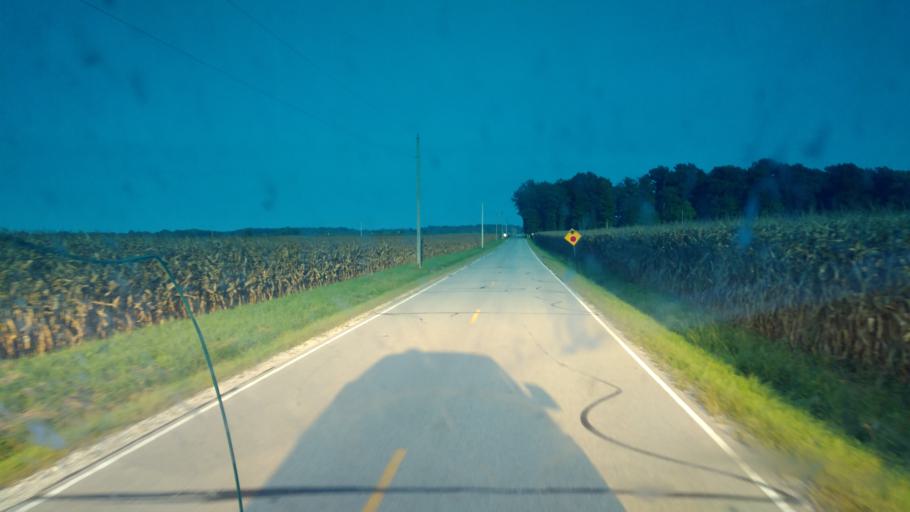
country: US
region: Ohio
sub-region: Crawford County
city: Galion
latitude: 40.8290
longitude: -82.8411
